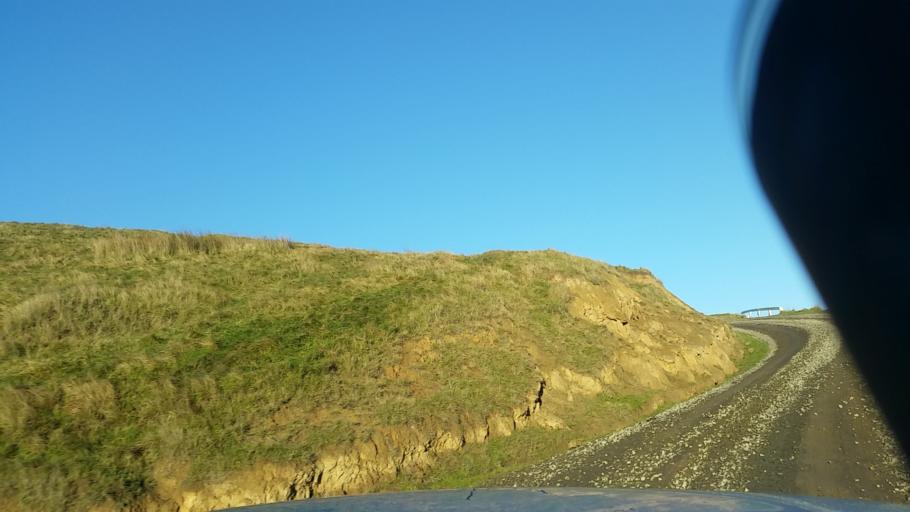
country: NZ
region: Canterbury
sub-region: Christchurch City
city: Christchurch
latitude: -43.7246
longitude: 173.0998
